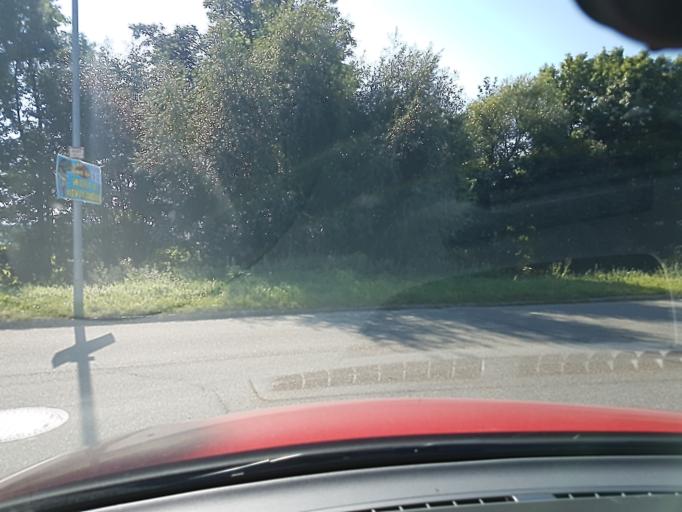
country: DE
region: Baden-Wuerttemberg
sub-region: Regierungsbezirk Stuttgart
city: Cleebronn
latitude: 49.0682
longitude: 9.0372
